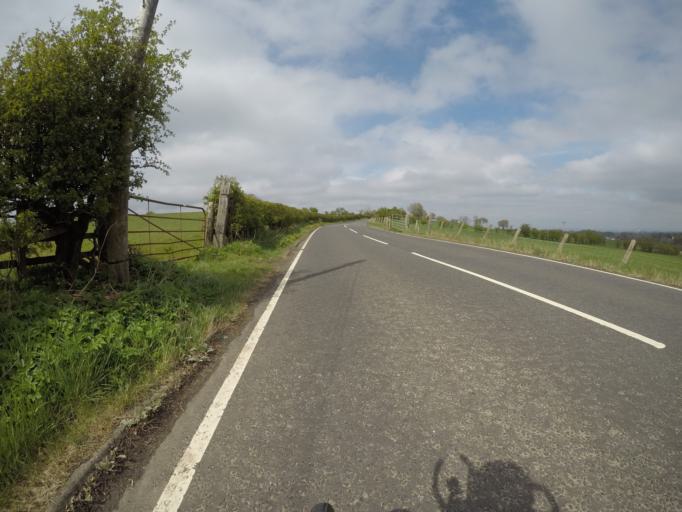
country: GB
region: Scotland
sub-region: East Renfrewshire
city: Barrhead
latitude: 55.7673
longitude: -4.3739
